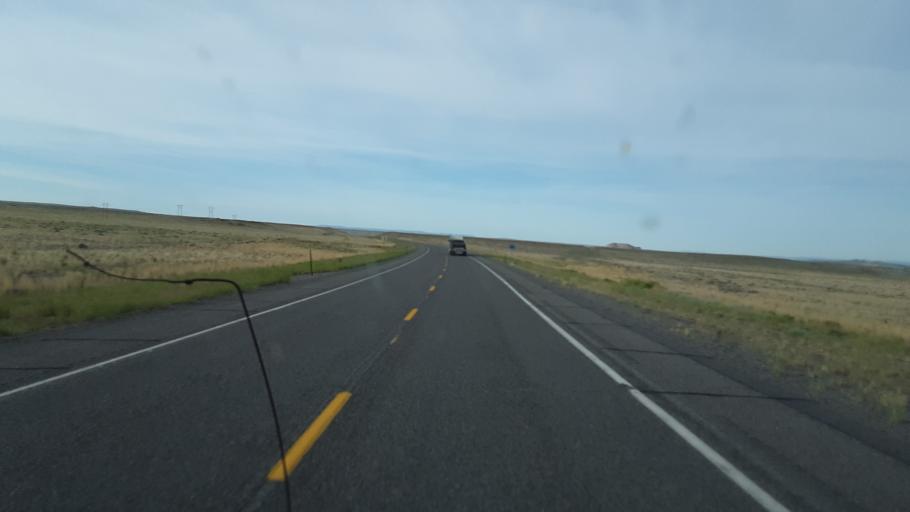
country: US
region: Wyoming
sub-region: Hot Springs County
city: Thermopolis
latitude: 43.2983
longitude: -108.1289
